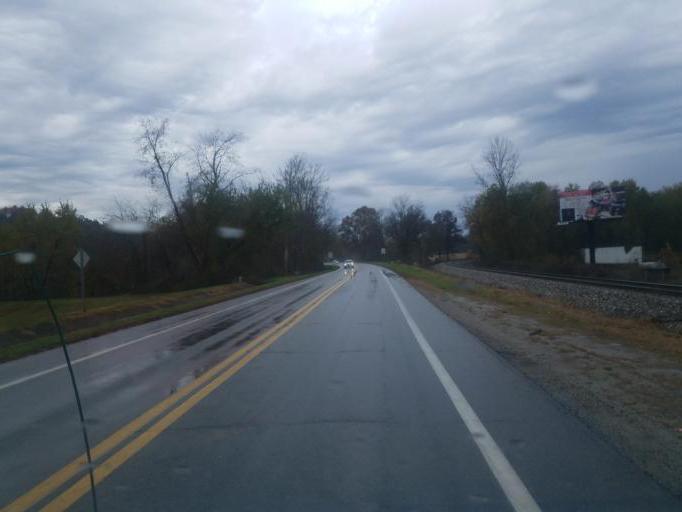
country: US
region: West Virginia
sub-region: Wood County
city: Williamstown
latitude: 39.3932
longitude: -81.4718
